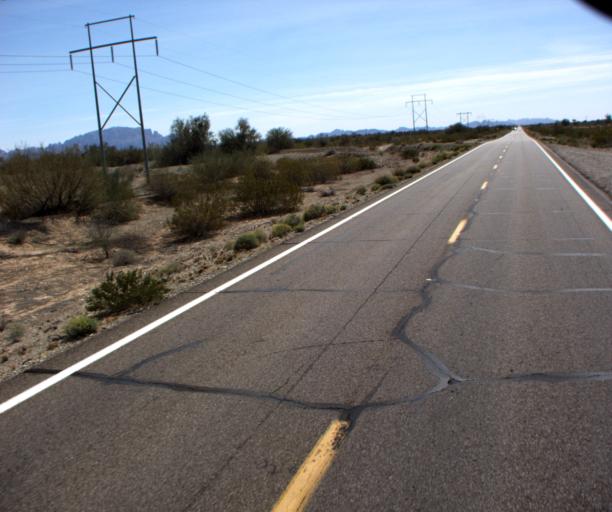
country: US
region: Arizona
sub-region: La Paz County
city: Quartzsite
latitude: 33.5137
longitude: -114.2170
